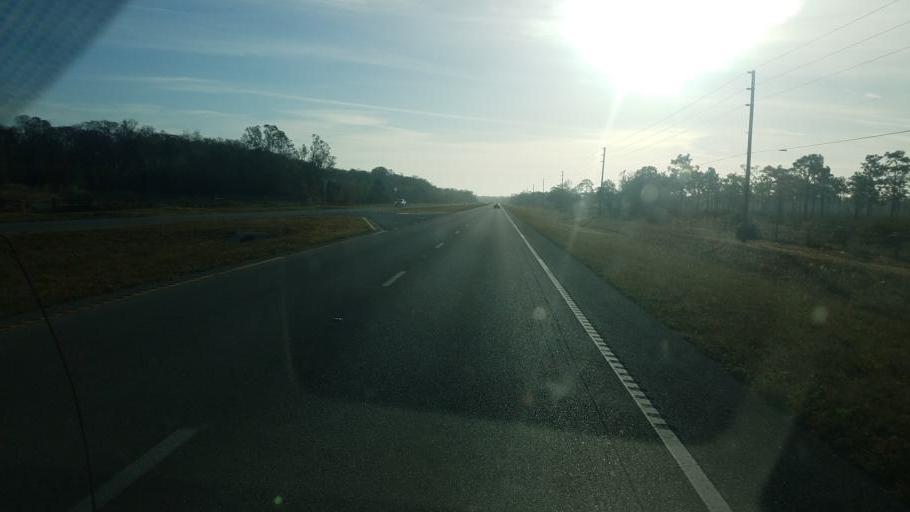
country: US
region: Florida
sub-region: Osceola County
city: Saint Cloud
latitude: 28.1361
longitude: -81.0309
